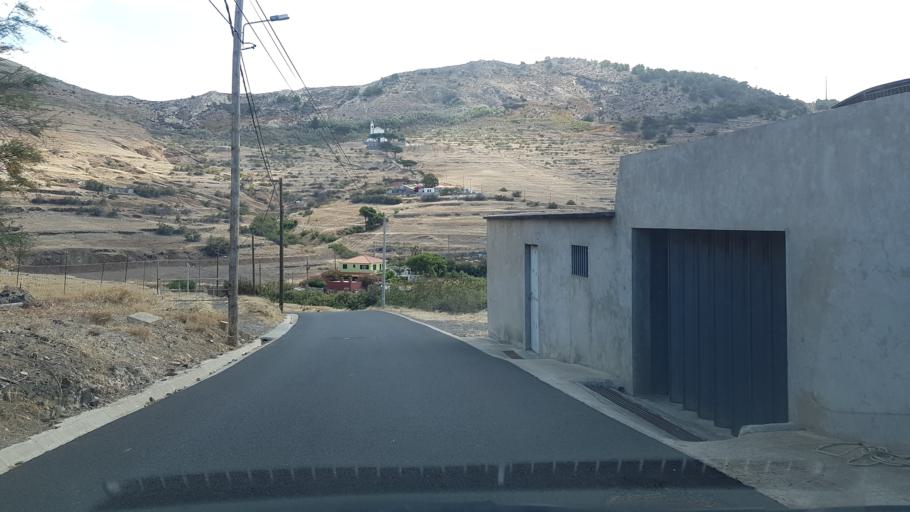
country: PT
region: Madeira
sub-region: Porto Santo
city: Vila de Porto Santo
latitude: 33.0712
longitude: -16.3295
